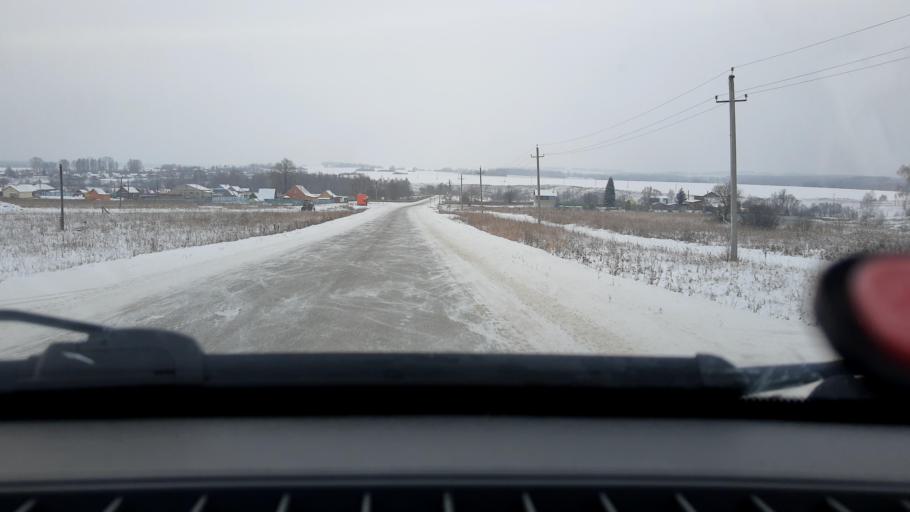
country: RU
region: Bashkortostan
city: Iglino
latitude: 54.6465
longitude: 56.4257
